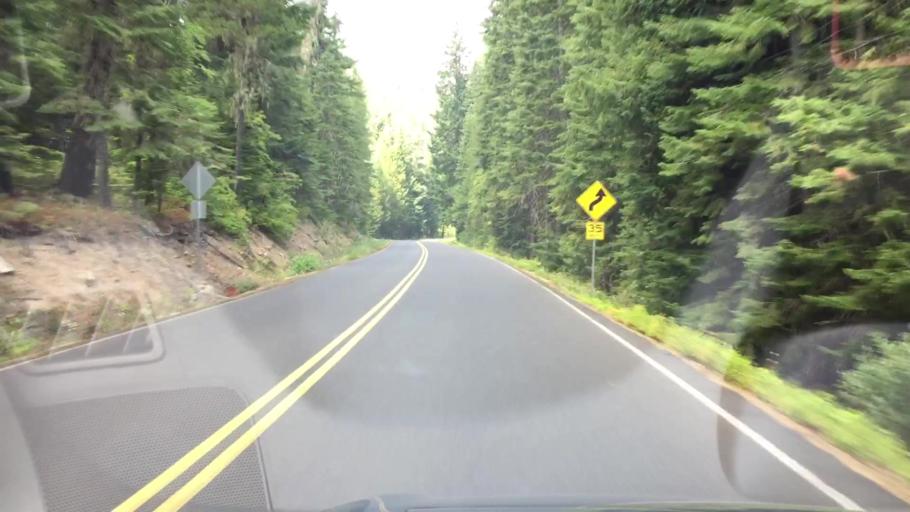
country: US
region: Washington
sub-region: Klickitat County
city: White Salmon
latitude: 46.0548
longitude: -121.5650
